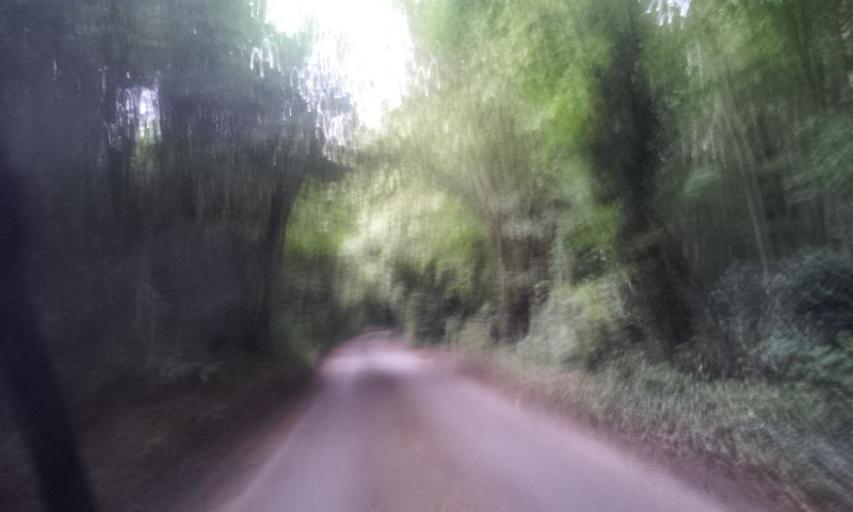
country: GB
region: England
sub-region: Kent
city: Wateringbury
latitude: 51.2671
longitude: 0.4551
